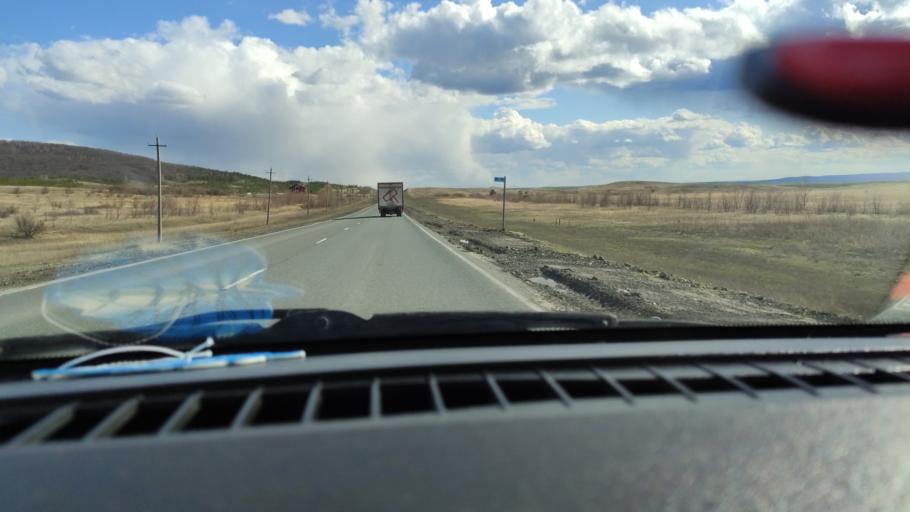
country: RU
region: Saratov
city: Alekseyevka
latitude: 52.3087
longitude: 47.9251
